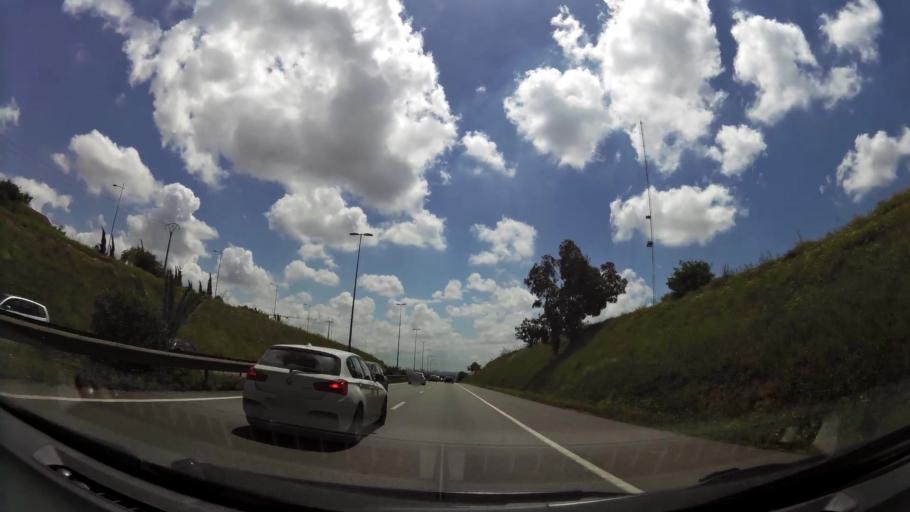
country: MA
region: Grand Casablanca
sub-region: Nouaceur
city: Bouskoura
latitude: 33.4928
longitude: -7.6299
